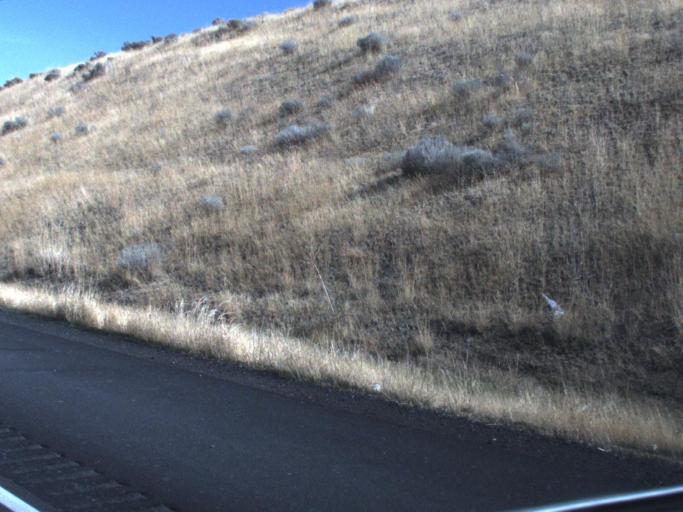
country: US
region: Washington
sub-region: Benton County
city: Prosser
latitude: 46.2207
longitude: -119.6859
